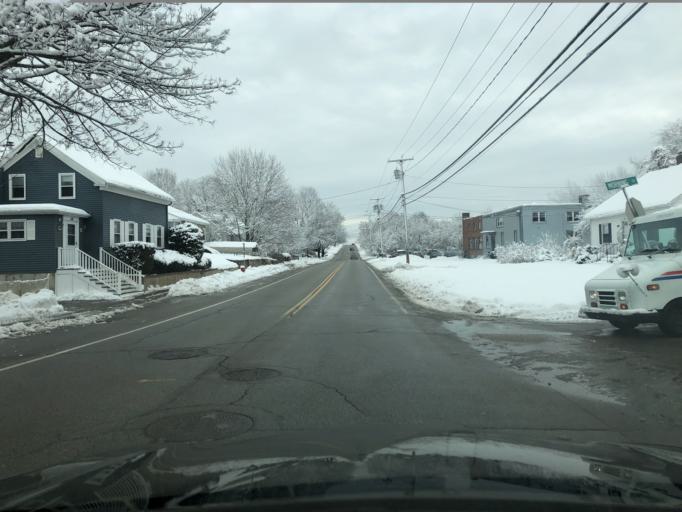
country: US
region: New Hampshire
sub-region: Strafford County
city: Somersworth
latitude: 43.2547
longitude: -70.8634
